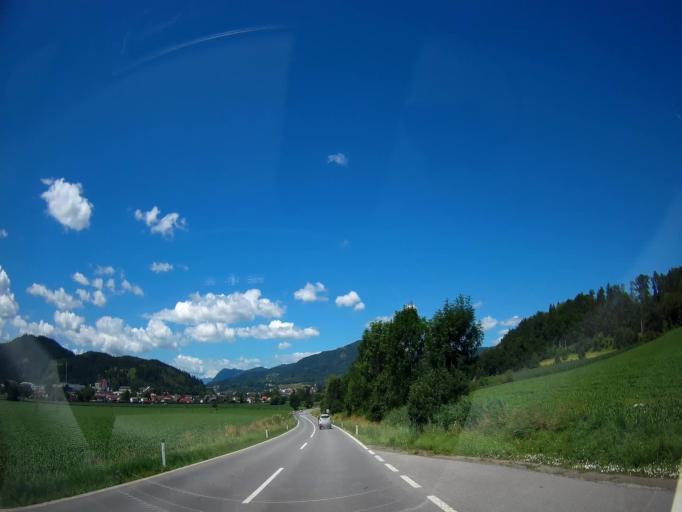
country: AT
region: Carinthia
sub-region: Politischer Bezirk Sankt Veit an der Glan
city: Sankt Veit an der Glan
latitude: 46.7631
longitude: 14.3908
